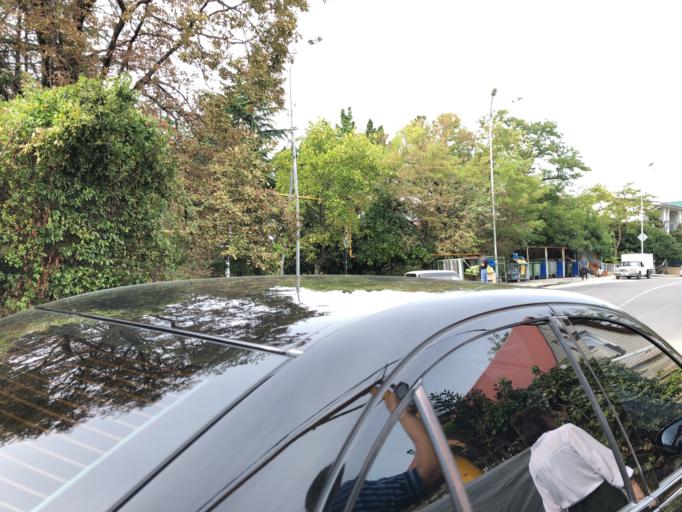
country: RU
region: Krasnodarskiy
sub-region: Sochi City
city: Sochi
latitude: 43.5934
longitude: 39.7418
